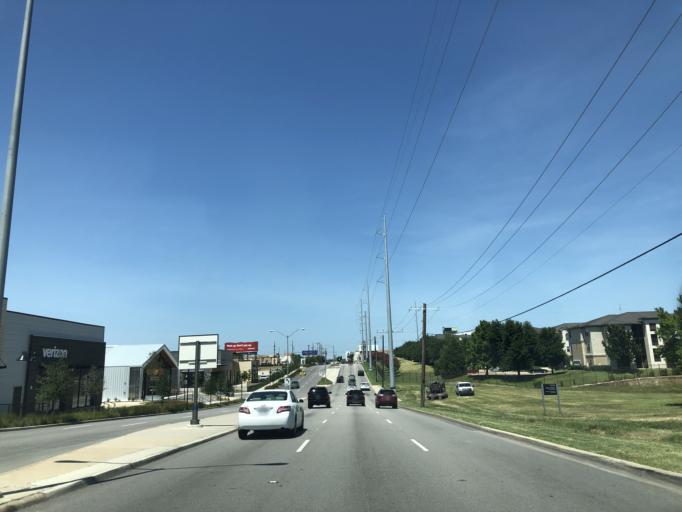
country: US
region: Texas
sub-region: Dallas County
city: University Park
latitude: 32.8260
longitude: -96.8469
